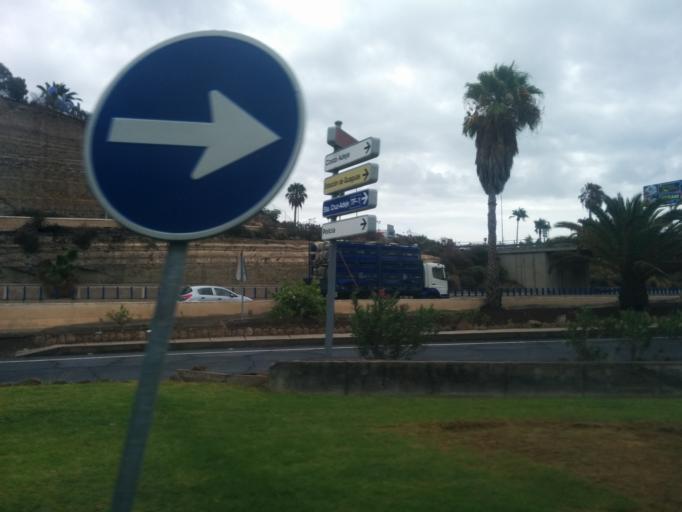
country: ES
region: Canary Islands
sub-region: Provincia de Santa Cruz de Tenerife
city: Playa de las Americas
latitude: 28.0818
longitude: -16.7295
